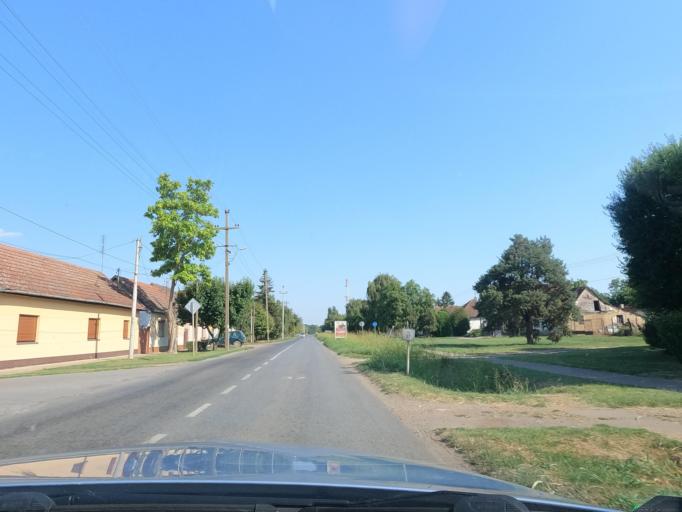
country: RS
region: Autonomna Pokrajina Vojvodina
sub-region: Juznobacki Okrug
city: Becej
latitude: 45.6267
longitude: 20.0255
